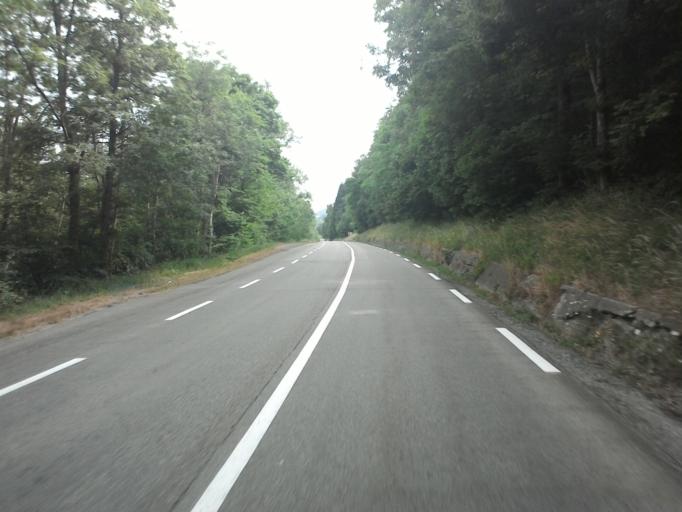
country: FR
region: Rhone-Alpes
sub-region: Departement de l'Isere
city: Notre-Dame-de-Mesage
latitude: 45.0121
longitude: 5.7731
